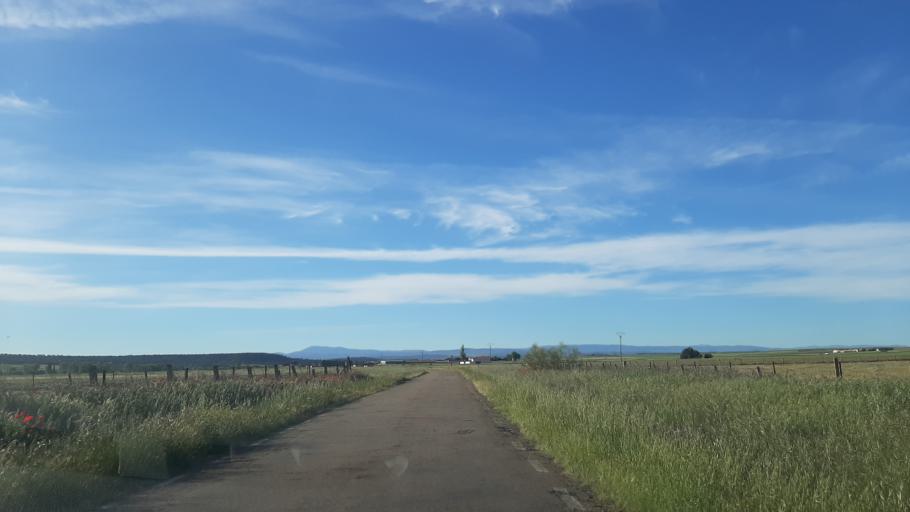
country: ES
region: Castille and Leon
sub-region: Provincia de Salamanca
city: Pedrosillo de Alba
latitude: 40.8171
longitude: -5.3900
